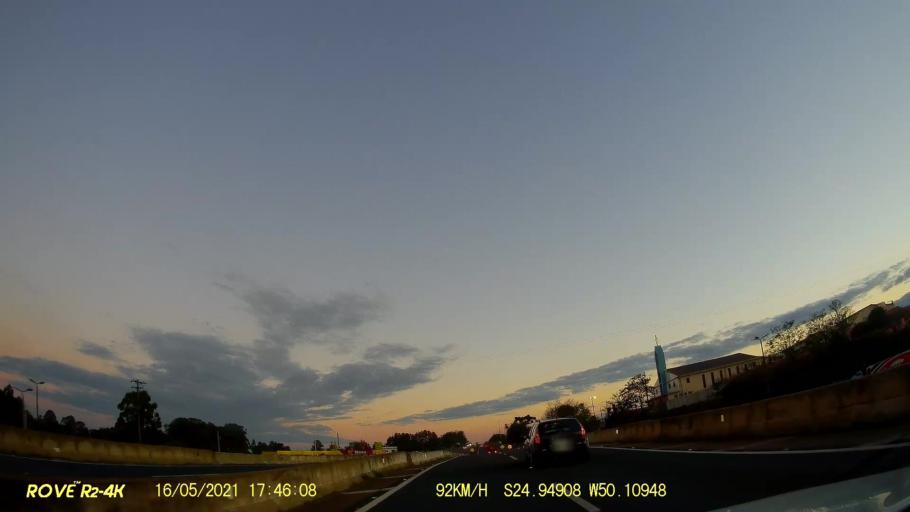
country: BR
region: Parana
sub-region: Carambei
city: Carambei
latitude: -24.9492
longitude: -50.1095
